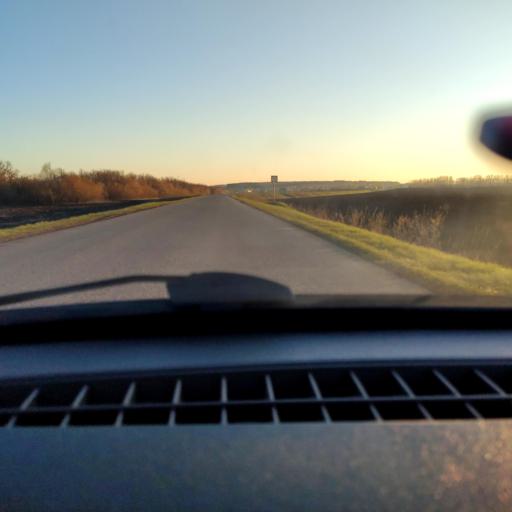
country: RU
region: Bashkortostan
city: Avdon
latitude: 54.5404
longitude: 55.6461
